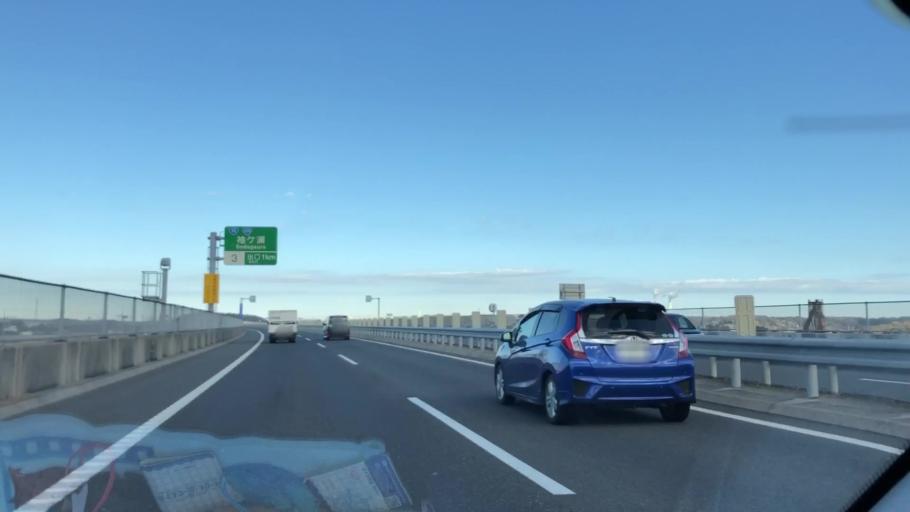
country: JP
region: Chiba
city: Kisarazu
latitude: 35.4009
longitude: 139.9666
